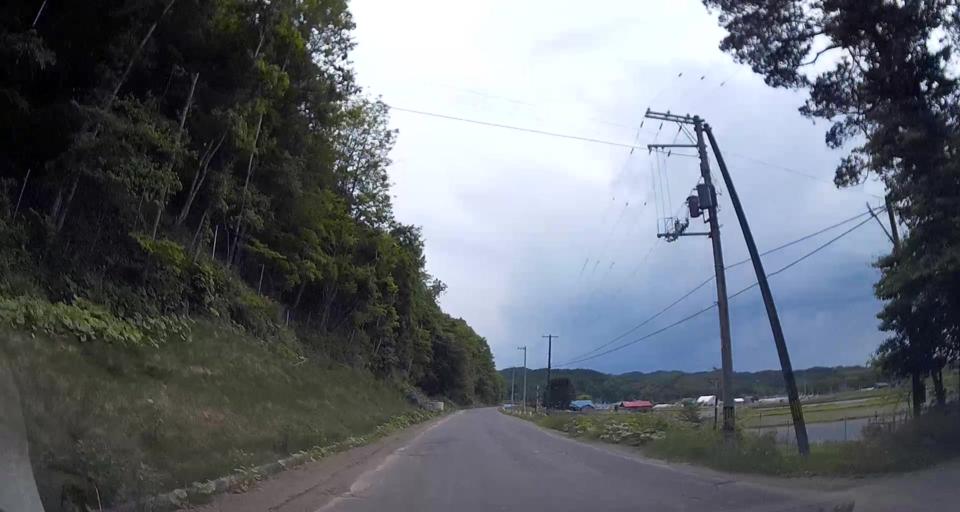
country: JP
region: Hokkaido
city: Chitose
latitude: 42.7587
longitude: 141.9794
